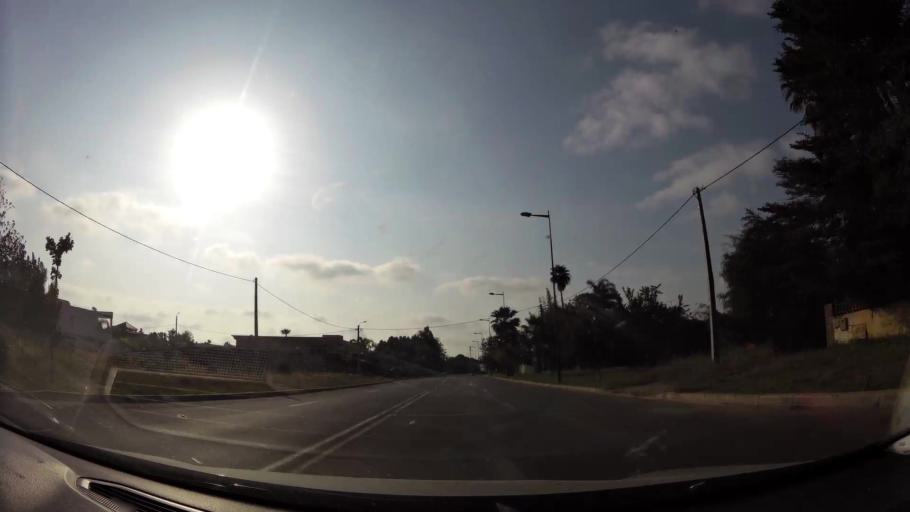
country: MA
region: Rabat-Sale-Zemmour-Zaer
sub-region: Rabat
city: Rabat
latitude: 33.9352
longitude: -6.8156
